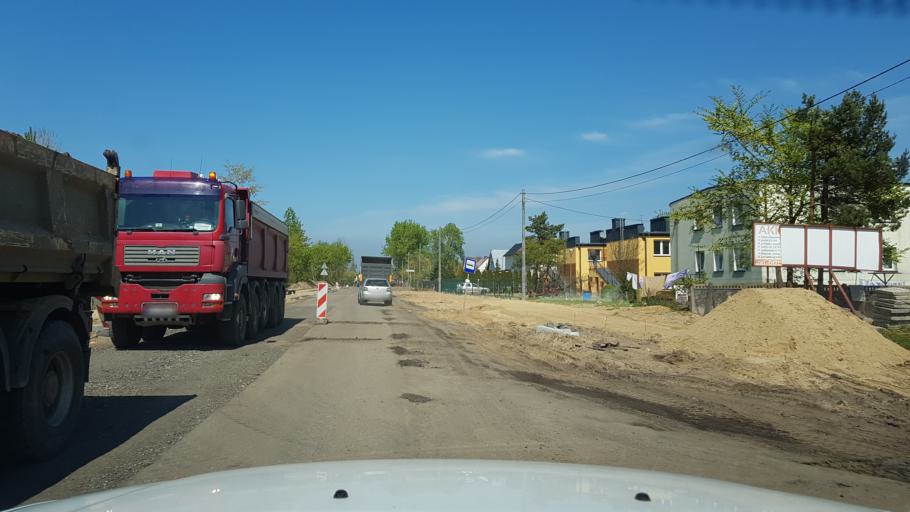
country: PL
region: Pomeranian Voivodeship
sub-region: Powiat slupski
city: Ustka
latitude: 54.5670
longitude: 16.8493
